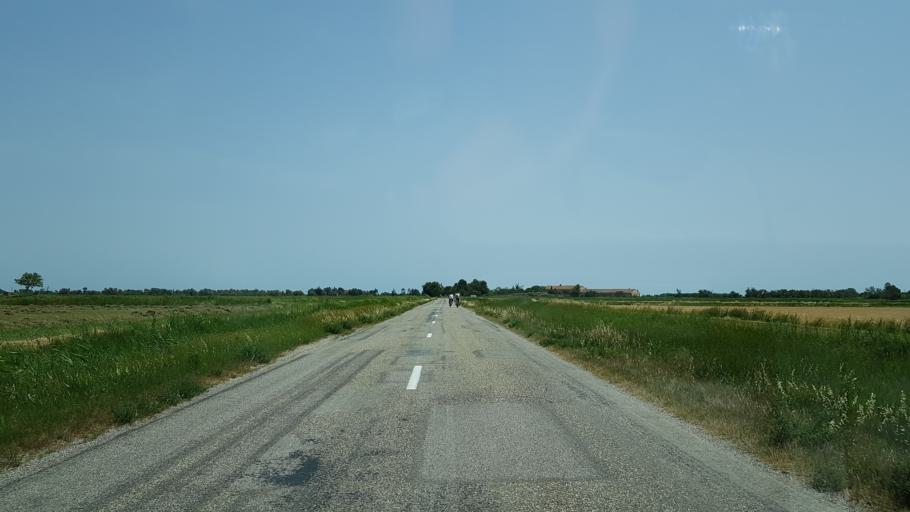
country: FR
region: Provence-Alpes-Cote d'Azur
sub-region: Departement des Bouches-du-Rhone
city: Port-Saint-Louis-du-Rhone
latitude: 43.4346
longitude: 4.6857
